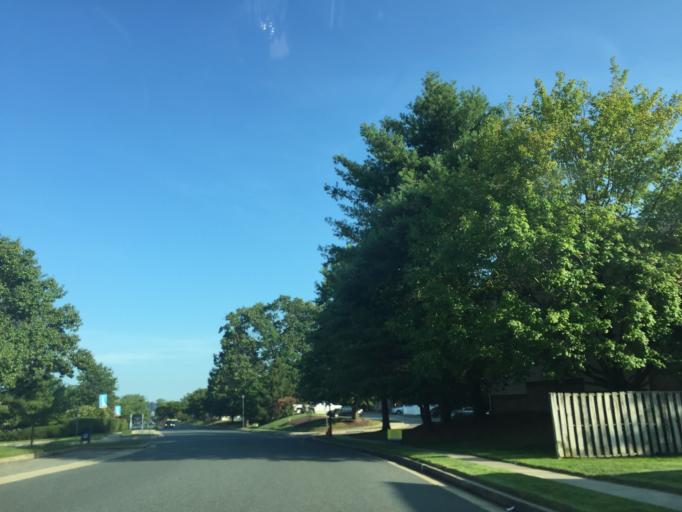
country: US
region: Maryland
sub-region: Baltimore County
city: Perry Hall
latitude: 39.3924
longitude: -76.4759
